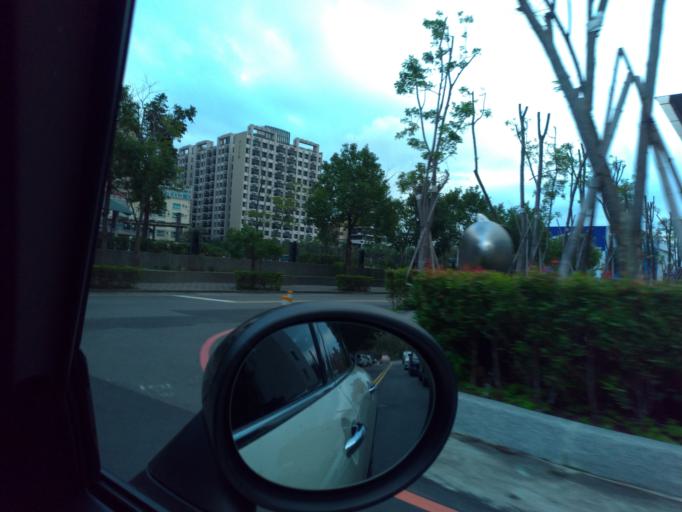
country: TW
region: Taiwan
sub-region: Hsinchu
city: Zhubei
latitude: 24.8055
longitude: 121.0314
